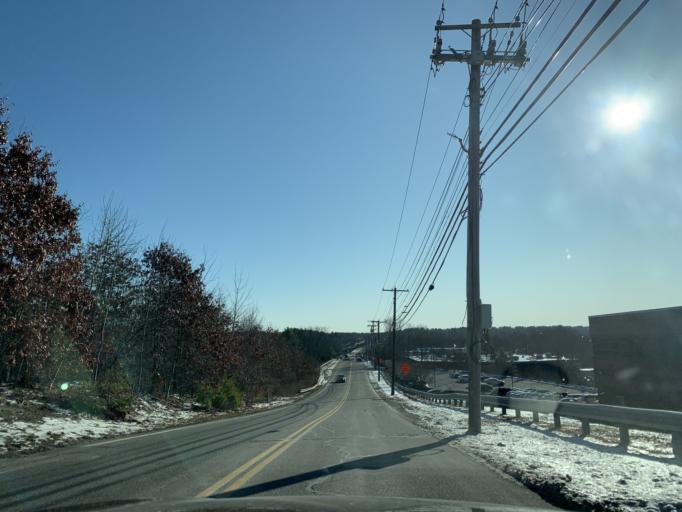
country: US
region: Massachusetts
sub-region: Norfolk County
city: Norwood
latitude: 42.2006
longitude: -71.1611
